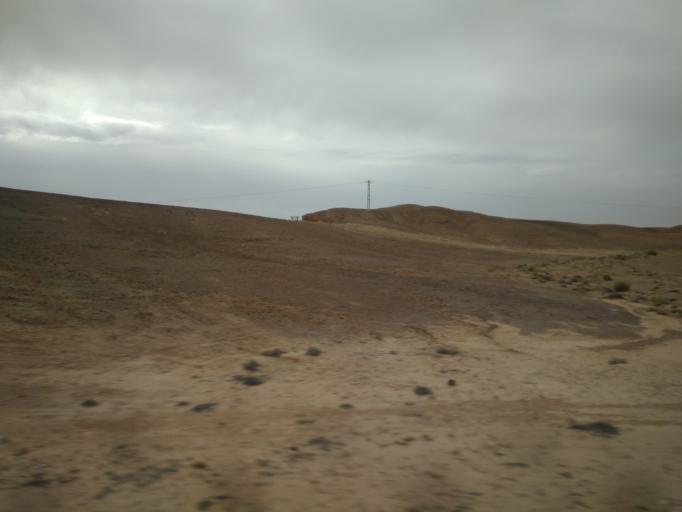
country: IL
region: Southern District
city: Eilat
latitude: 29.8900
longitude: 34.8558
